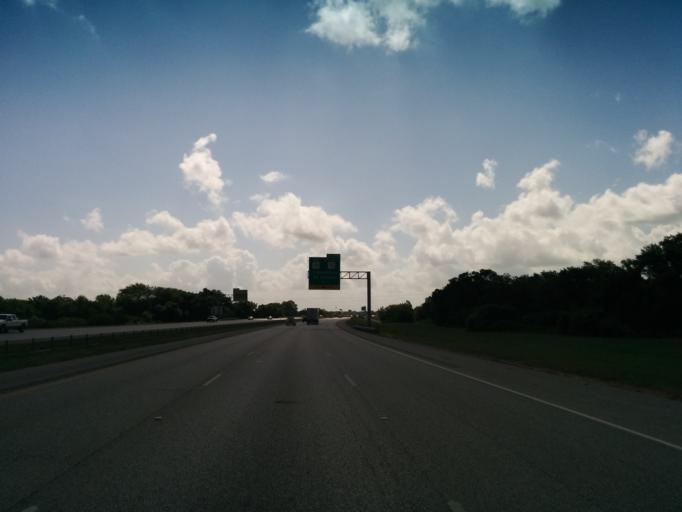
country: US
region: Texas
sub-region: Colorado County
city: Columbus
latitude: 29.6936
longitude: -96.5611
